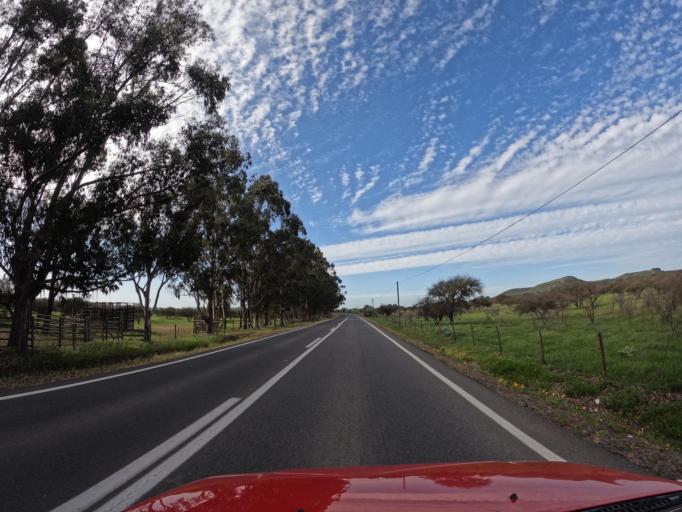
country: CL
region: Valparaiso
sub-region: San Antonio Province
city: San Antonio
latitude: -34.1717
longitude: -71.7313
